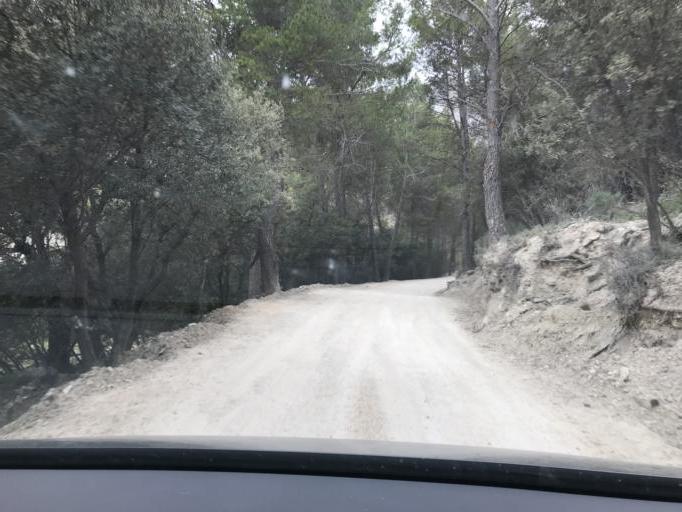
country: ES
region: Andalusia
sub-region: Provincia de Granada
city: Castril
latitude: 37.8398
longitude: -2.7746
